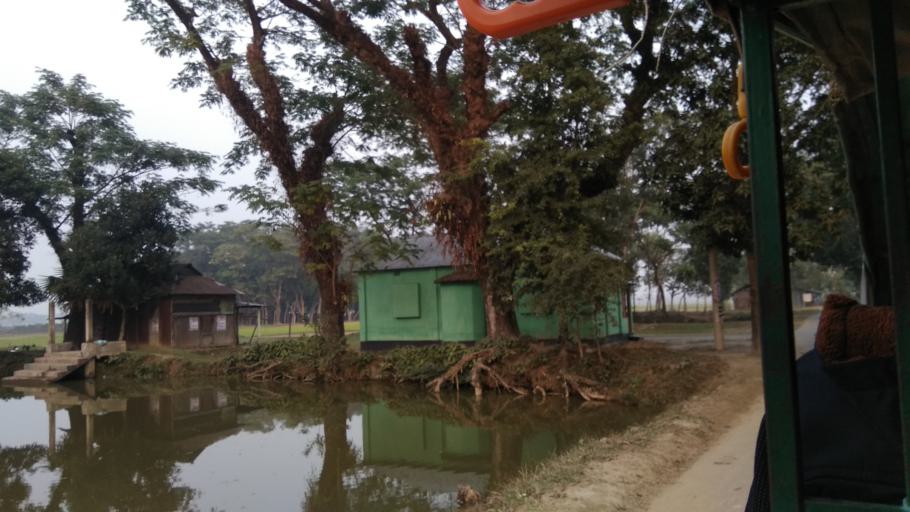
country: BD
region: Dhaka
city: Netrakona
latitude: 24.8854
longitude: 90.6678
